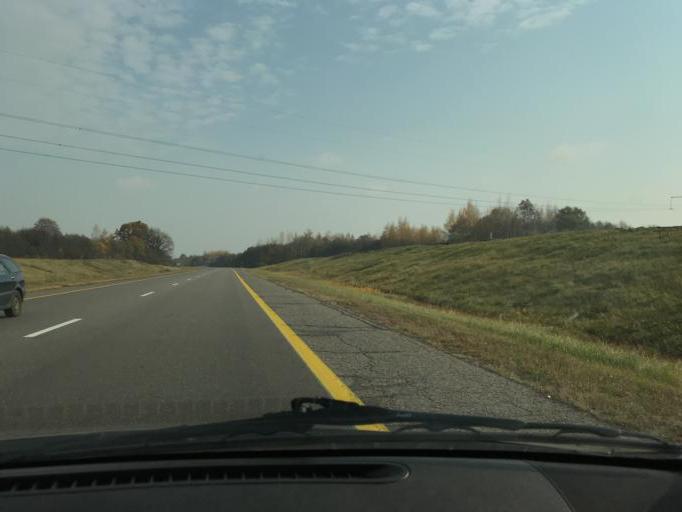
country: BY
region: Vitebsk
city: Chashniki
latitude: 54.9954
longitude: 28.9413
